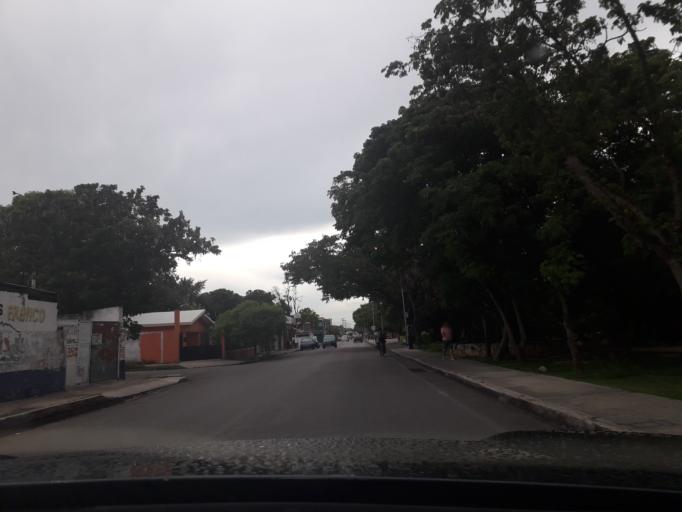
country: MX
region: Yucatan
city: Merida
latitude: 20.9764
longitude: -89.6556
